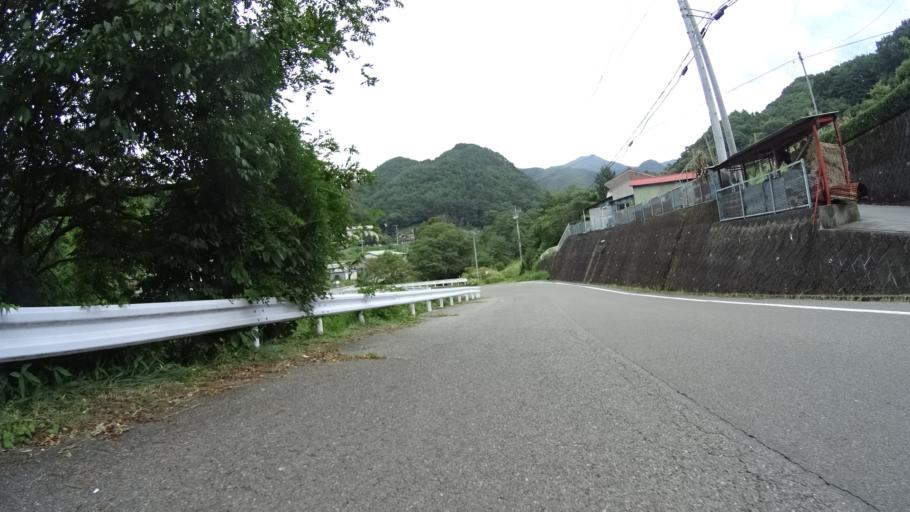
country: JP
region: Yamanashi
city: Nirasaki
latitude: 35.8635
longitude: 138.5245
